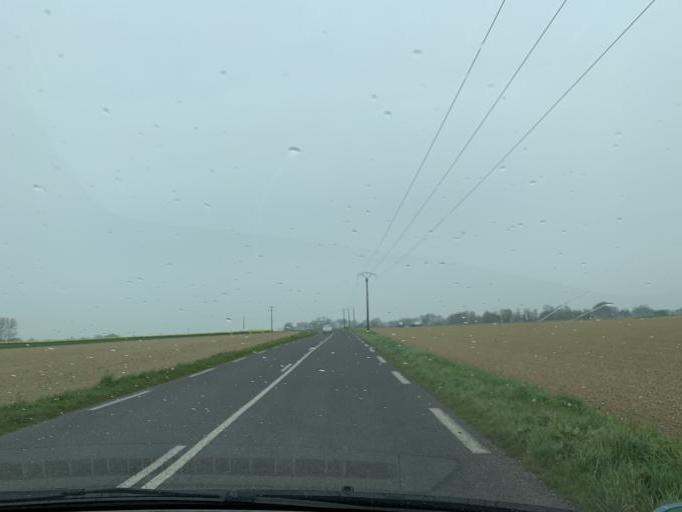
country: FR
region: Haute-Normandie
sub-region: Departement de la Seine-Maritime
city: Cany-Barville
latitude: 49.7931
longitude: 0.6609
